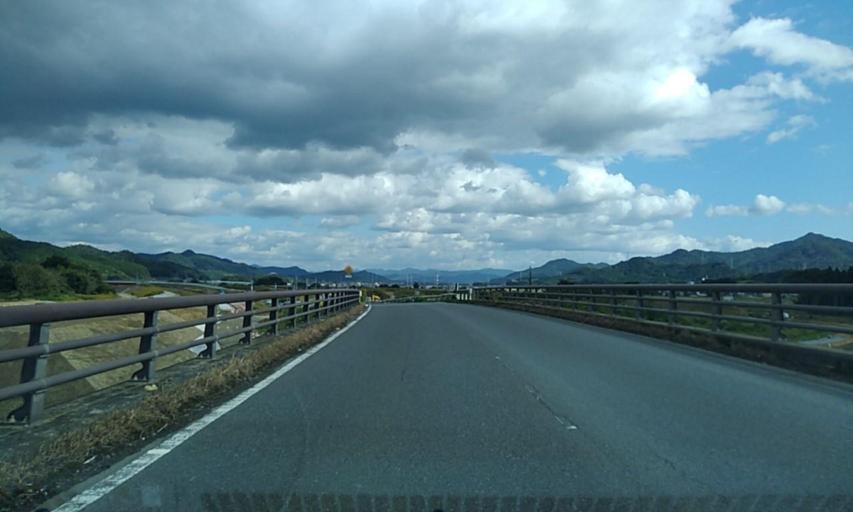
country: JP
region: Kyoto
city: Fukuchiyama
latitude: 35.3032
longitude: 135.1545
